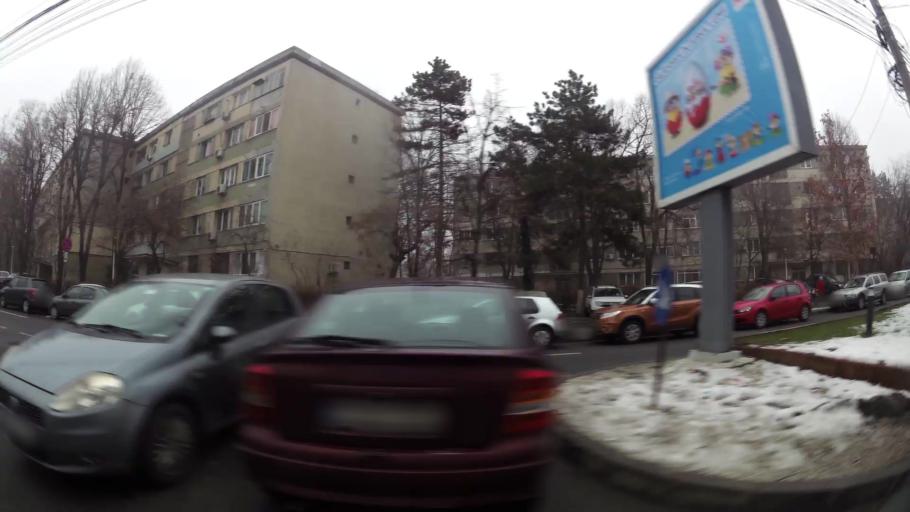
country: RO
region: Ilfov
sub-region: Comuna Chiajna
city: Rosu
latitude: 44.4587
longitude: 26.0406
